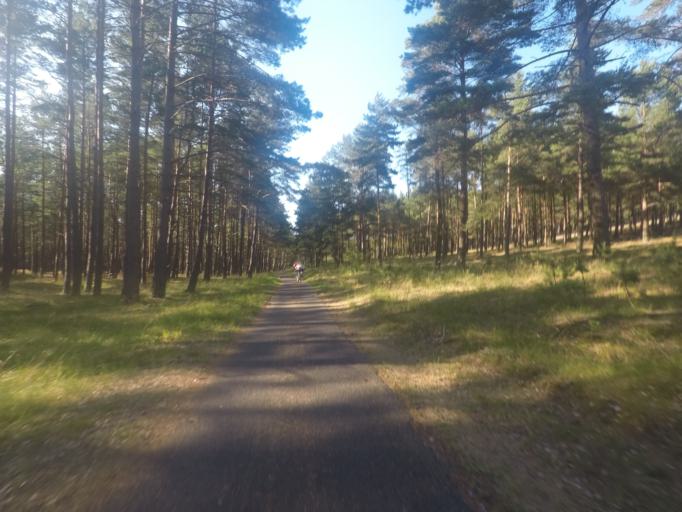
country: LT
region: Klaipedos apskritis
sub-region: Klaipeda
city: Klaipeda
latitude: 55.5790
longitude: 21.1142
